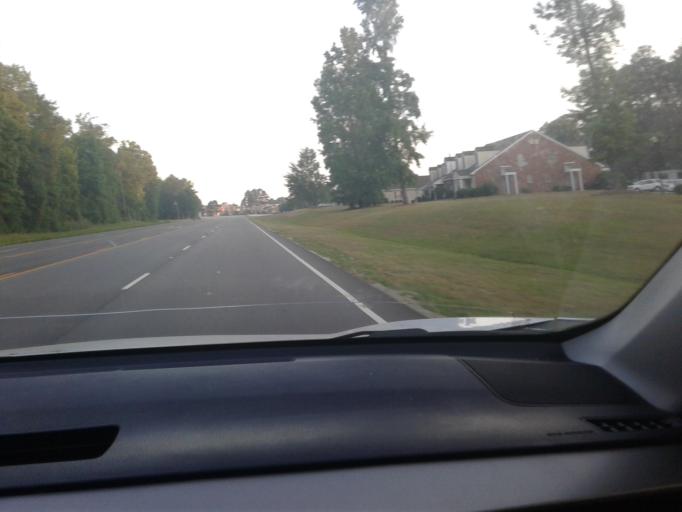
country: US
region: North Carolina
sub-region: Harnett County
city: Buies Creek
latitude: 35.4009
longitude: -78.7355
